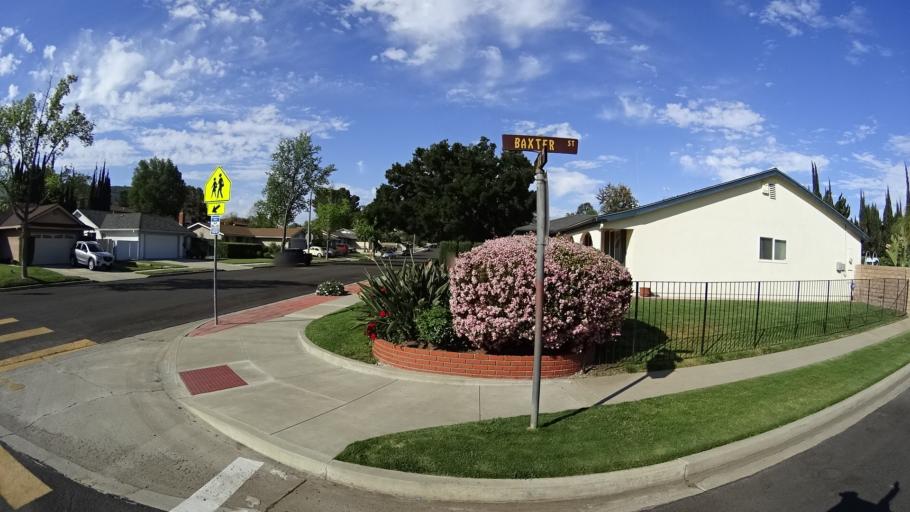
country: US
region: California
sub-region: Ventura County
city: Casa Conejo
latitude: 34.1748
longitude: -118.9512
